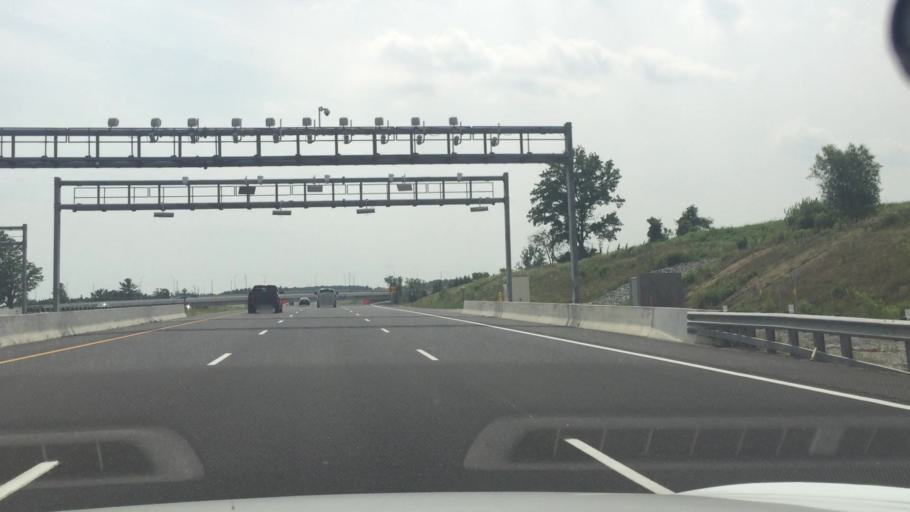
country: CA
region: Ontario
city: Pickering
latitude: 43.9263
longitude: -79.0902
